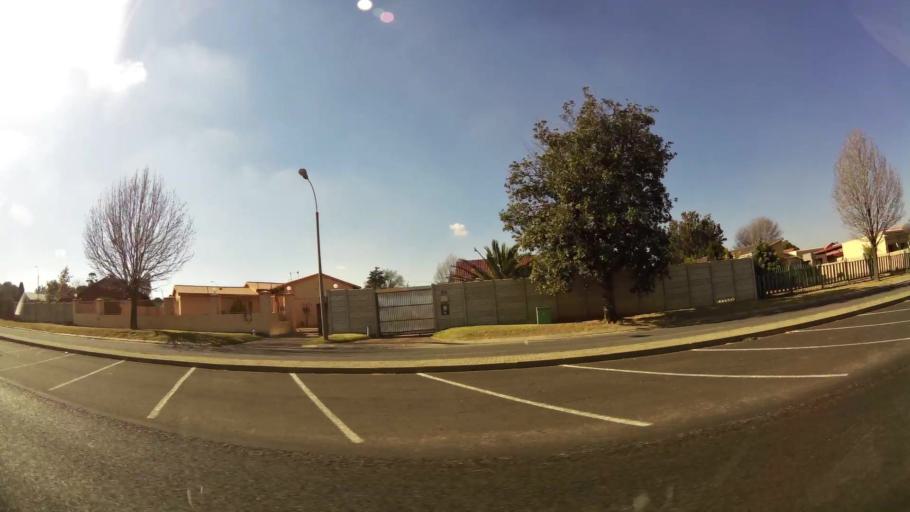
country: ZA
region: Gauteng
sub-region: City of Johannesburg Metropolitan Municipality
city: Roodepoort
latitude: -26.1479
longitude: 27.8235
